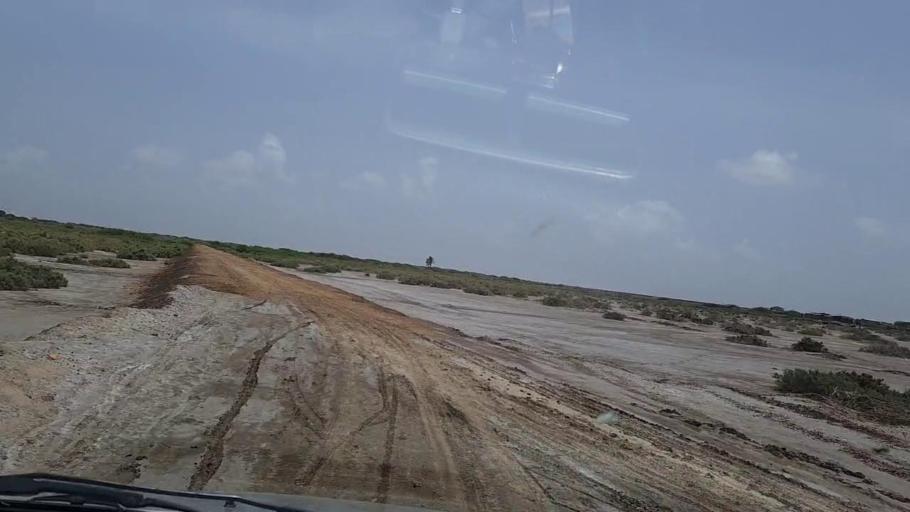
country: PK
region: Sindh
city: Keti Bandar
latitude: 24.1560
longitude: 67.5288
